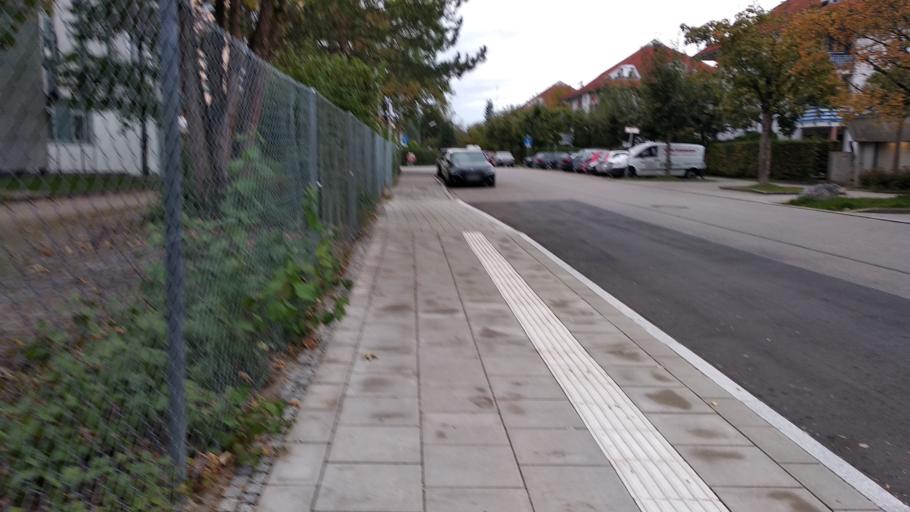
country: DE
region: Bavaria
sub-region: Upper Bavaria
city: Putzbrunn
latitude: 48.0772
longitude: 11.7198
